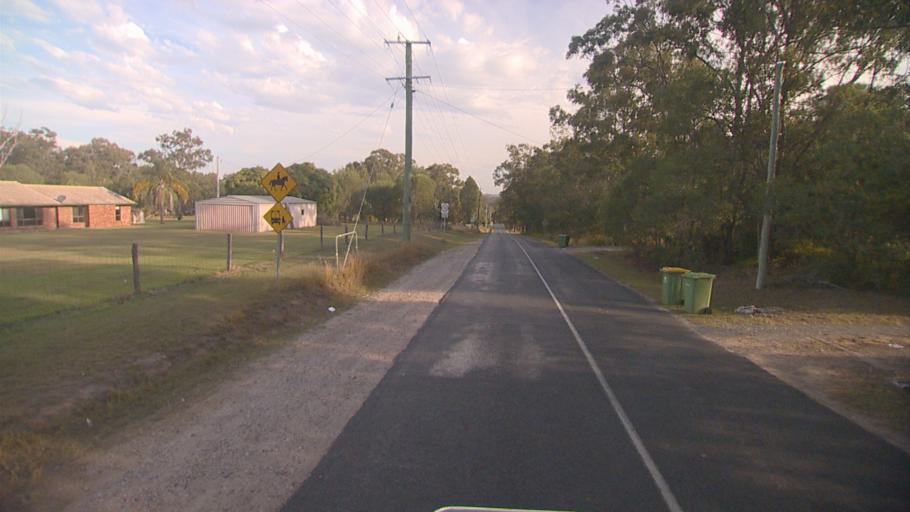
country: AU
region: Queensland
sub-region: Logan
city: Chambers Flat
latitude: -27.8365
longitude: 153.1074
